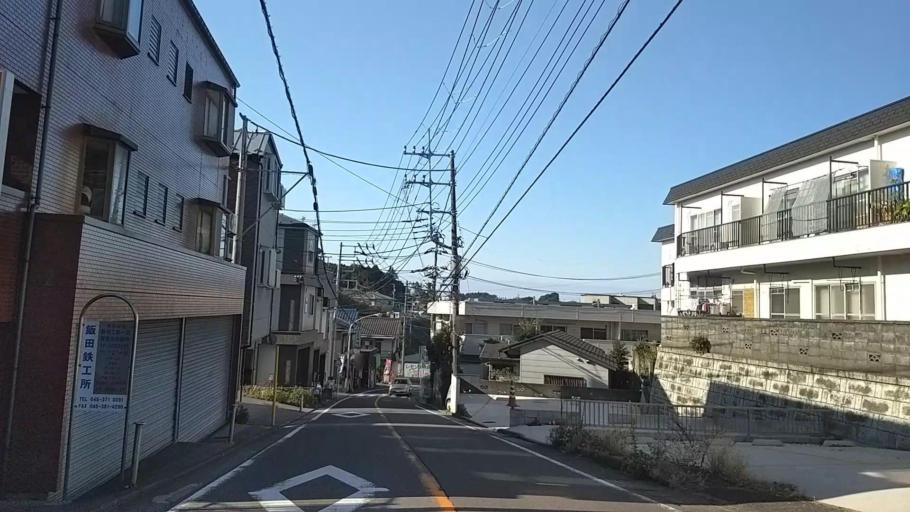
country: JP
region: Kanagawa
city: Yokohama
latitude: 35.4637
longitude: 139.5679
